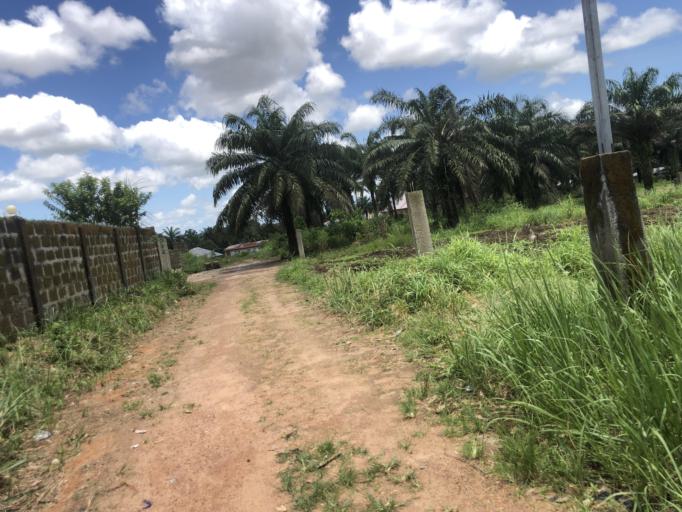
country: SL
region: Northern Province
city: Makeni
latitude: 8.8588
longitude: -12.0437
